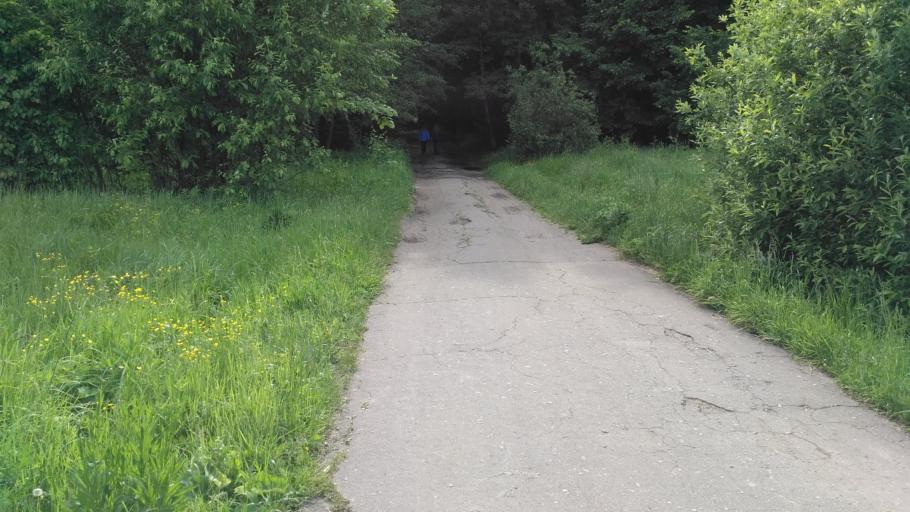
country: RU
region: Moscow
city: Metrogorodok
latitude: 55.8337
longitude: 37.7640
